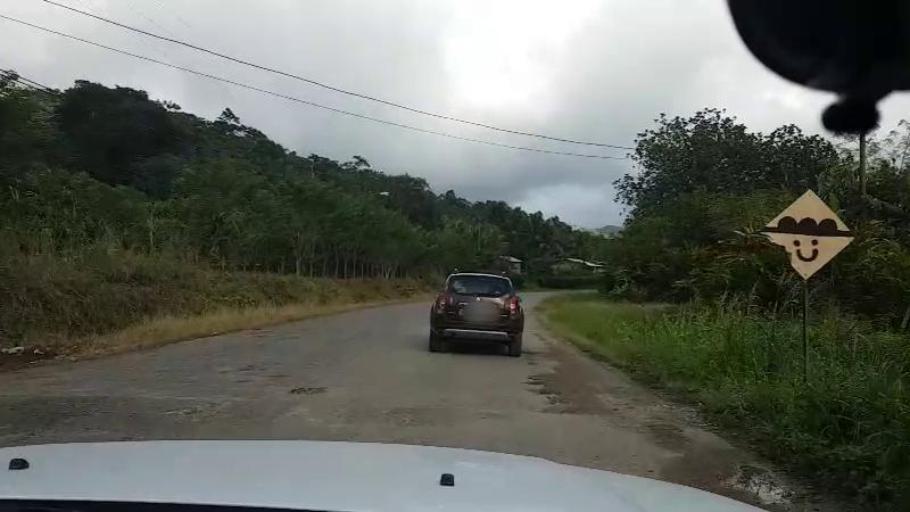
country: BZ
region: Stann Creek
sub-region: Dangriga
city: Dangriga
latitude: 17.0004
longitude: -88.4220
